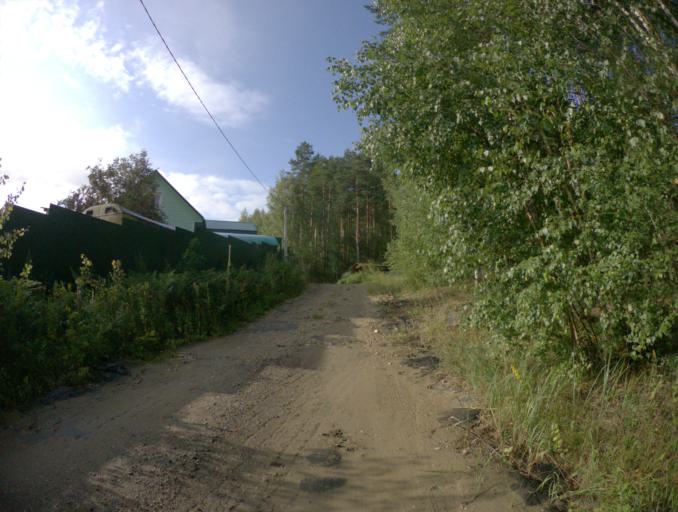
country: RU
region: Vladimir
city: Raduzhnyy
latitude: 56.0079
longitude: 40.2726
